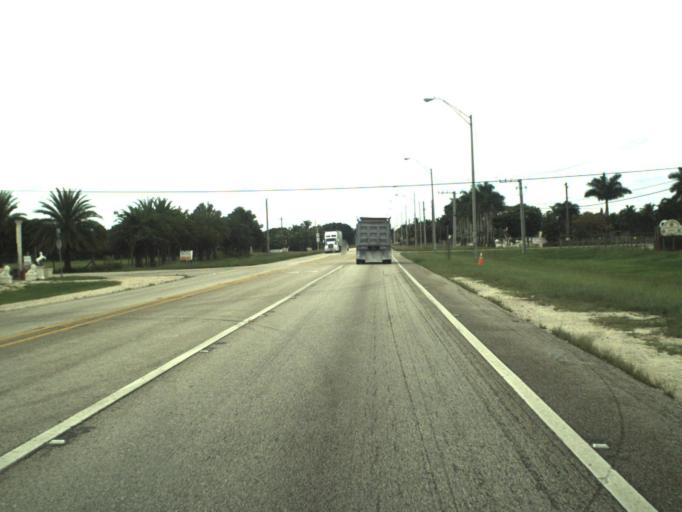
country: US
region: Florida
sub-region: Miami-Dade County
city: Richmond West
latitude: 25.6102
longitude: -80.4791
